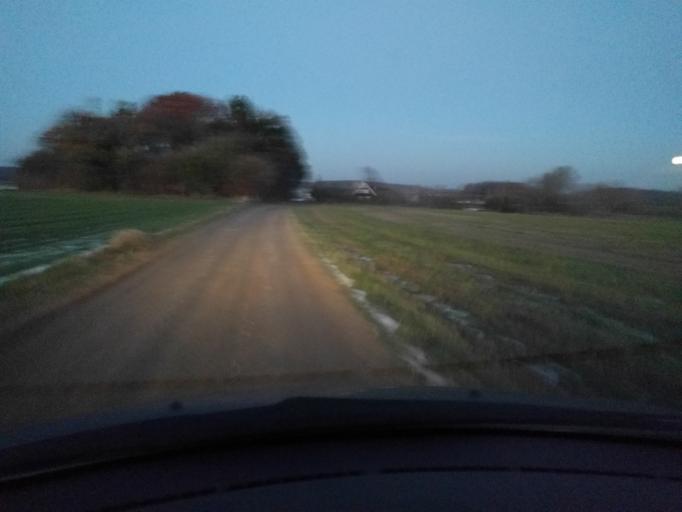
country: DK
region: South Denmark
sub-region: Kerteminde Kommune
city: Langeskov
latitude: 55.4087
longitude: 10.6036
